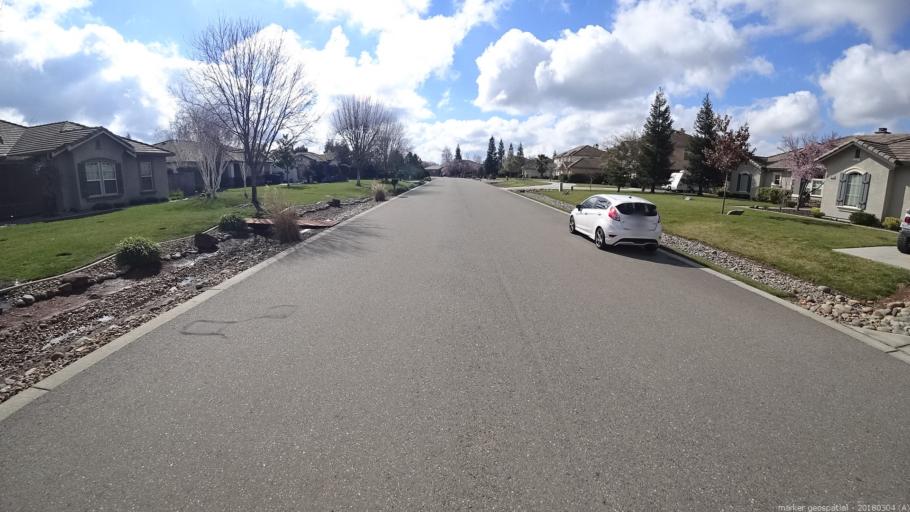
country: US
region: California
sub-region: Sacramento County
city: Vineyard
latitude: 38.4668
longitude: -121.3148
